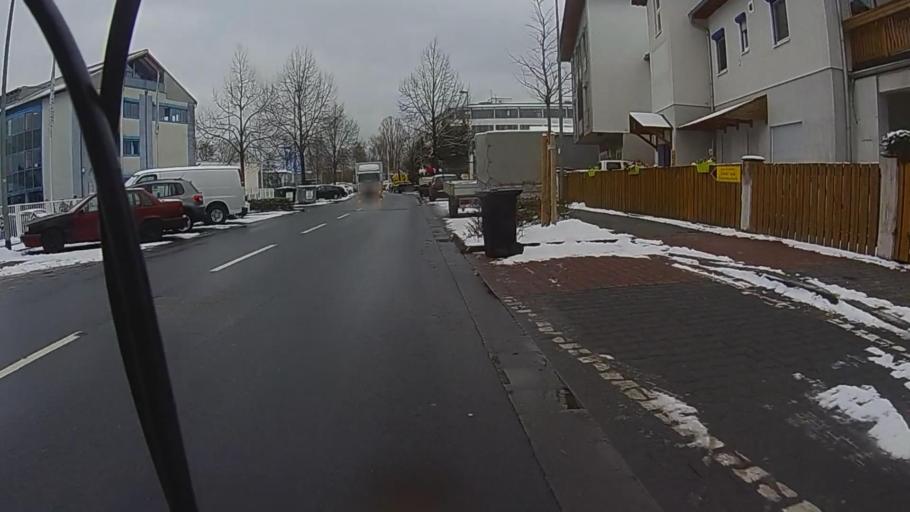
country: DE
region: Hesse
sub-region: Regierungsbezirk Darmstadt
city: Oberursel
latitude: 50.1886
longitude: 8.5880
